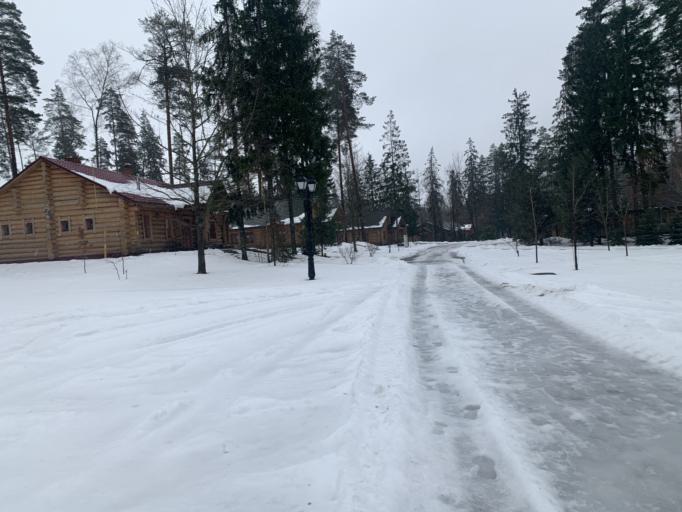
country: BY
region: Minsk
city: Slabada
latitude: 53.9489
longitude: 27.9836
